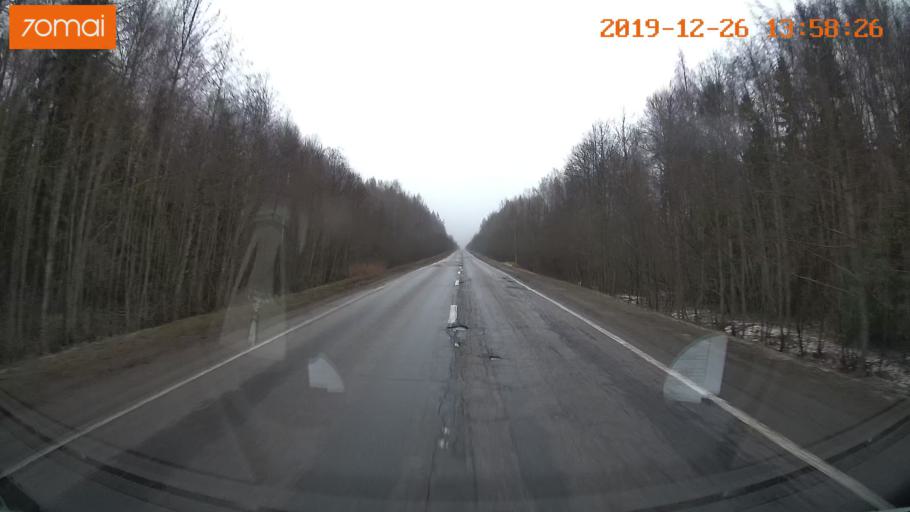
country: RU
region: Jaroslavl
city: Poshekhon'ye
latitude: 58.5741
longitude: 38.7008
